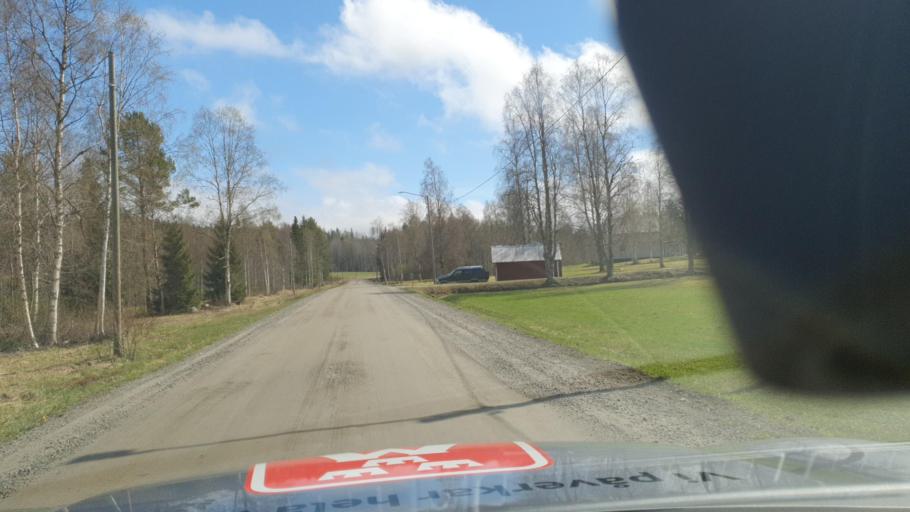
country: SE
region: Vaesterbotten
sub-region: Bjurholms Kommun
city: Bjurholm
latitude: 63.6966
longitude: 18.9521
